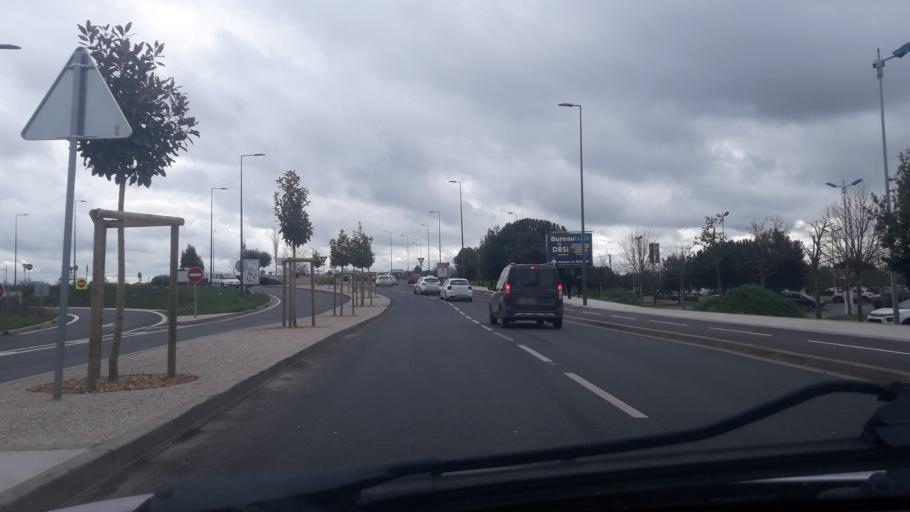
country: FR
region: Midi-Pyrenees
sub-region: Departement de la Haute-Garonne
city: Tournefeuille
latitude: 43.6085
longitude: 1.3073
